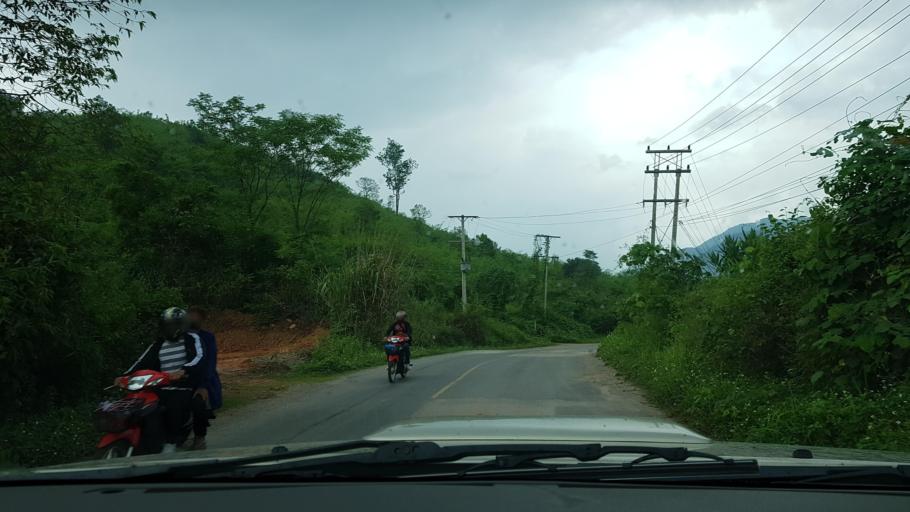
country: LA
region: Oudomxai
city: Muang Xay
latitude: 20.6219
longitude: 101.9582
